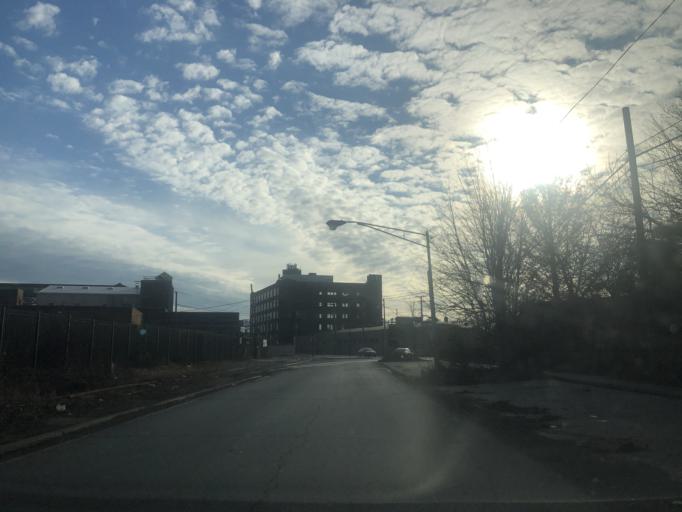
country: US
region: Illinois
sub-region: Cook County
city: Chicago
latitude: 41.9081
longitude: -87.6596
